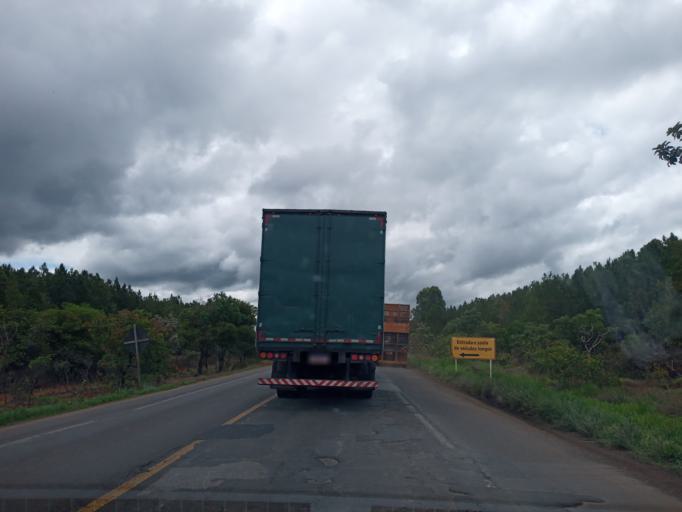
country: BR
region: Minas Gerais
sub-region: Uberaba
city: Uberaba
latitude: -19.2676
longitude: -47.7201
